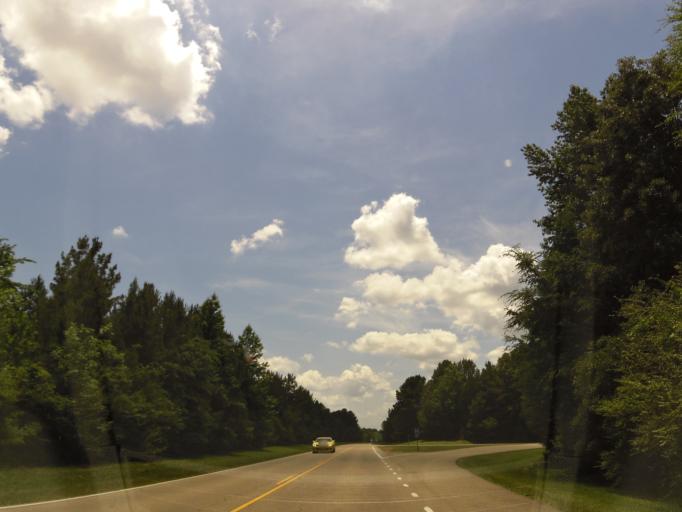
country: US
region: Mississippi
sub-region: Lee County
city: Verona
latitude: 34.2384
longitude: -88.7642
